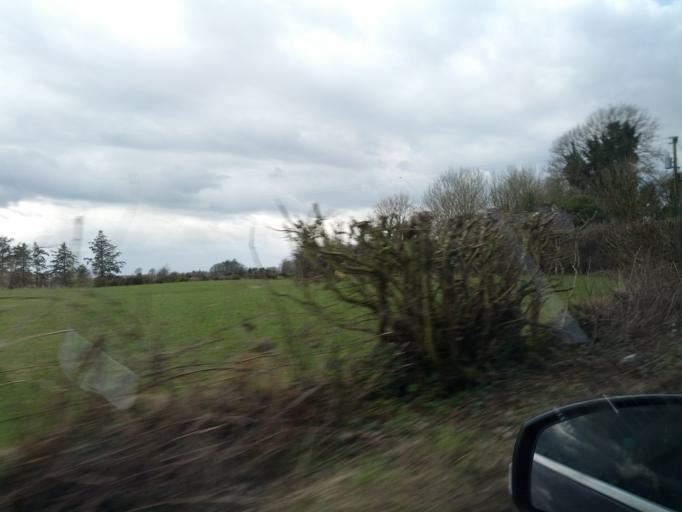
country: IE
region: Connaught
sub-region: County Galway
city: Athenry
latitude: 53.4925
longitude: -8.5958
